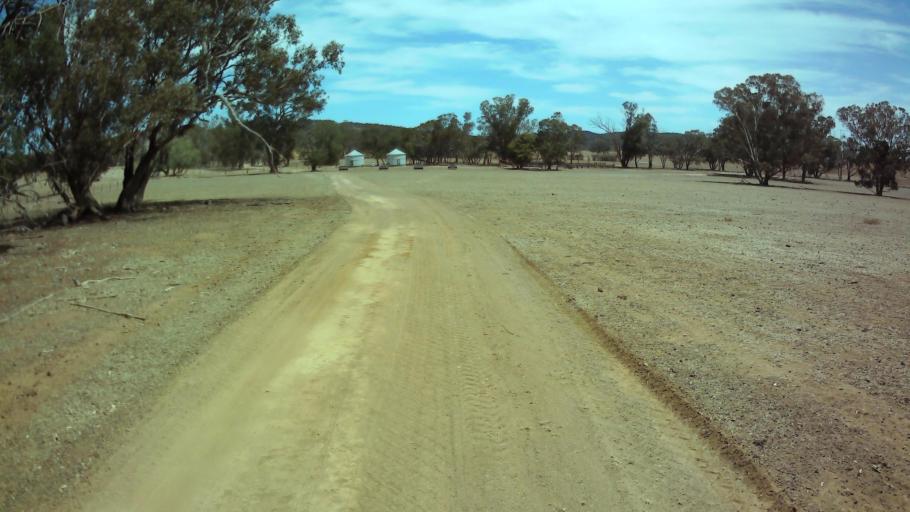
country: AU
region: New South Wales
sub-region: Weddin
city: Grenfell
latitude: -33.7759
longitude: 148.1517
